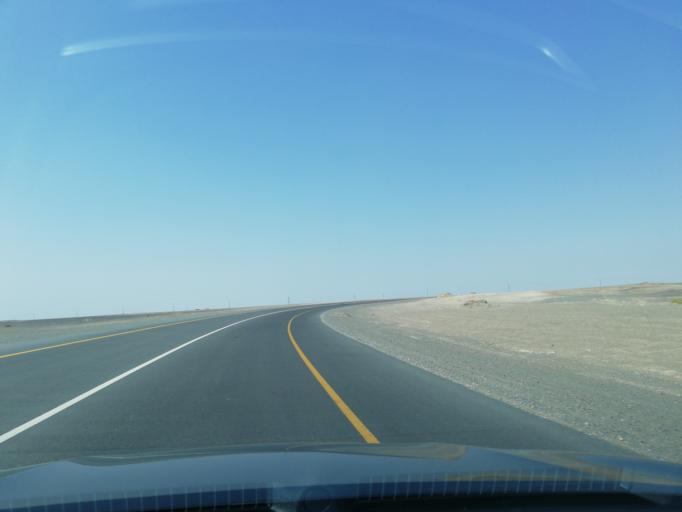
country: OM
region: Muhafazat ad Dakhiliyah
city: Adam
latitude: 22.2494
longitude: 58.0945
